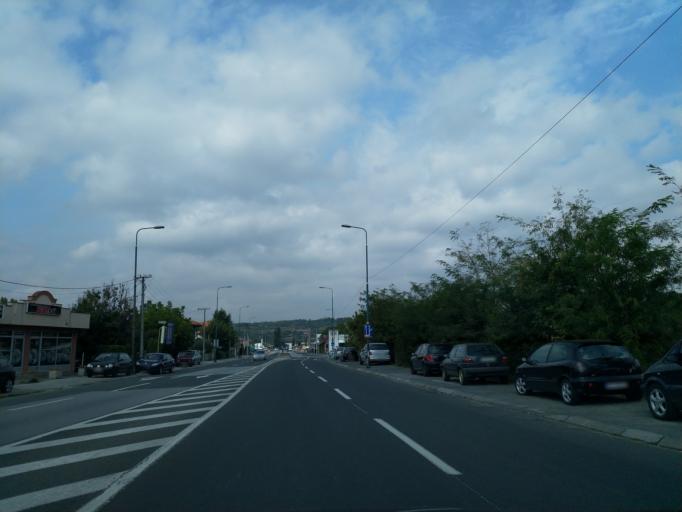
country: RS
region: Central Serbia
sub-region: Sumadijski Okrug
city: Kragujevac
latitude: 44.0380
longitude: 20.9105
